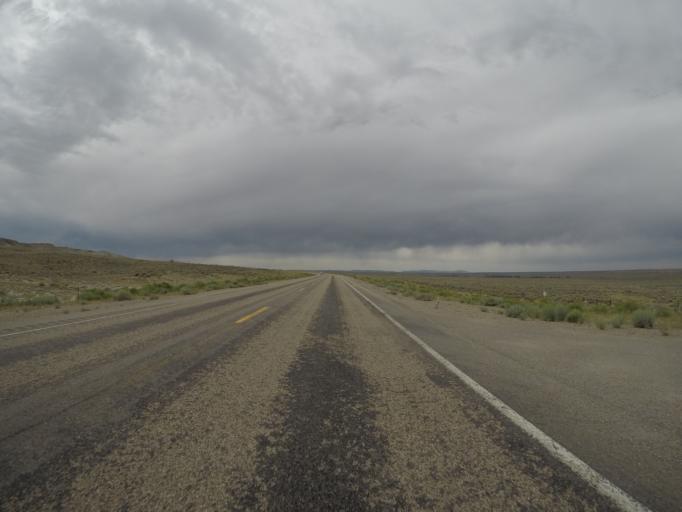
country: US
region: Wyoming
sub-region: Lincoln County
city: Kemmerer
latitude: 41.9485
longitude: -110.0138
